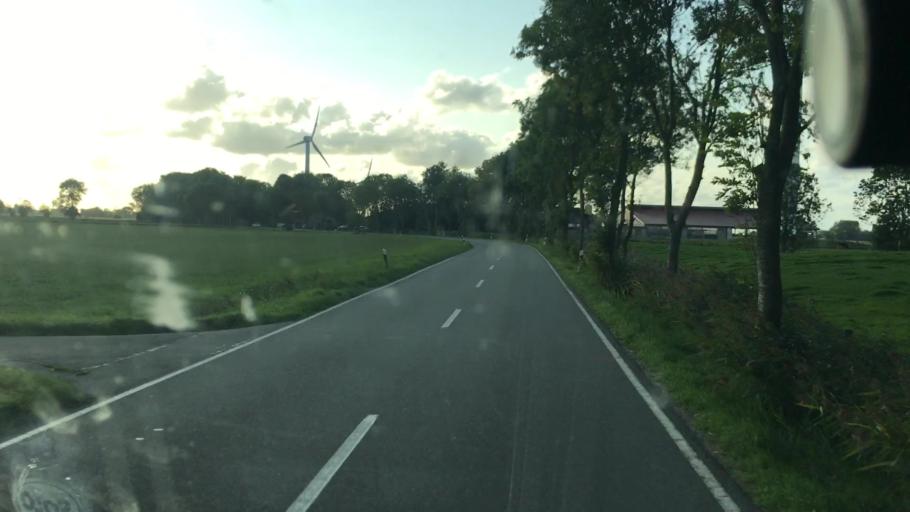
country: DE
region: Lower Saxony
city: Wittmund
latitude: 53.6426
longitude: 7.8138
